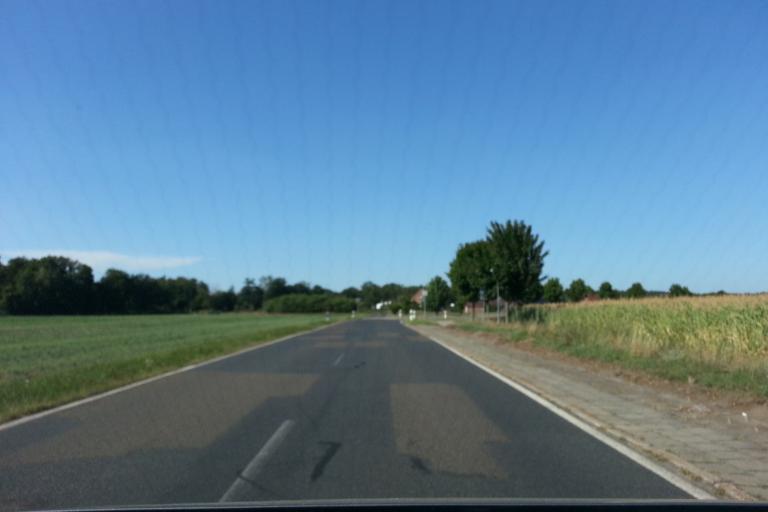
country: DE
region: Mecklenburg-Vorpommern
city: Eggesin
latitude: 53.6769
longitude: 14.0351
